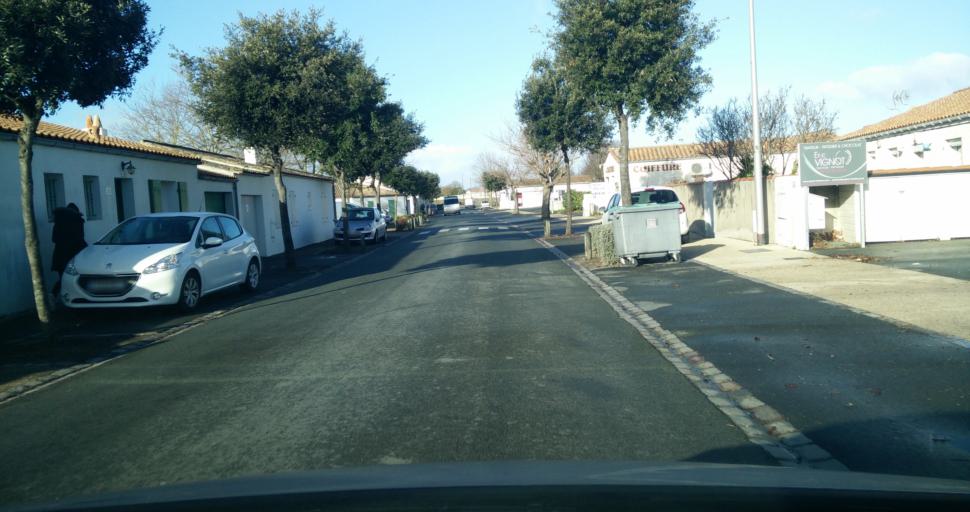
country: FR
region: Poitou-Charentes
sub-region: Departement de la Charente-Maritime
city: Saint-Martin-de-Re
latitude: 46.1979
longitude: -1.3582
